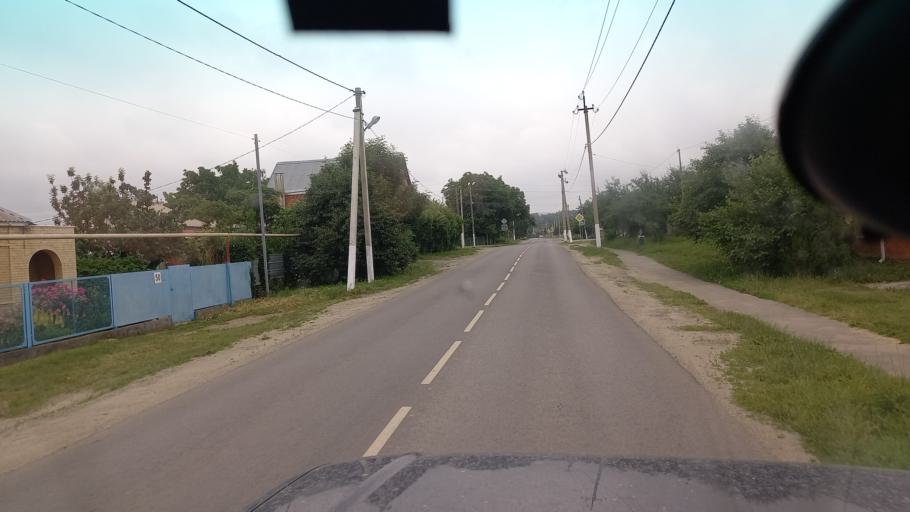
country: RU
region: Krasnodarskiy
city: Mostovskoy
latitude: 44.4151
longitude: 40.7939
